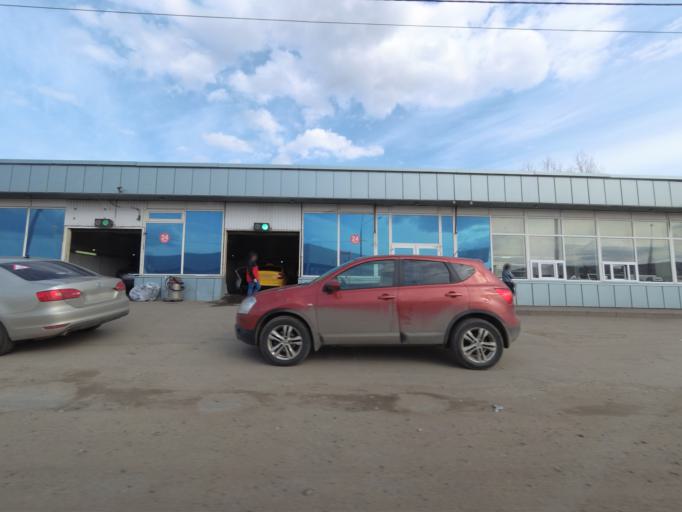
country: RU
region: Moskovskaya
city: Lobnya
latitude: 55.9873
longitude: 37.4168
